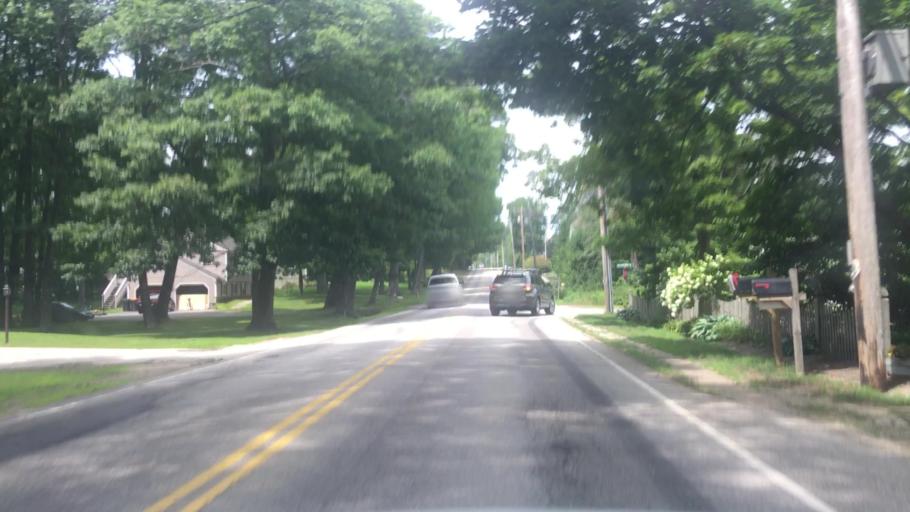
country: US
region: Maine
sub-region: Cumberland County
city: Scarborough
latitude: 43.5867
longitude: -70.2936
